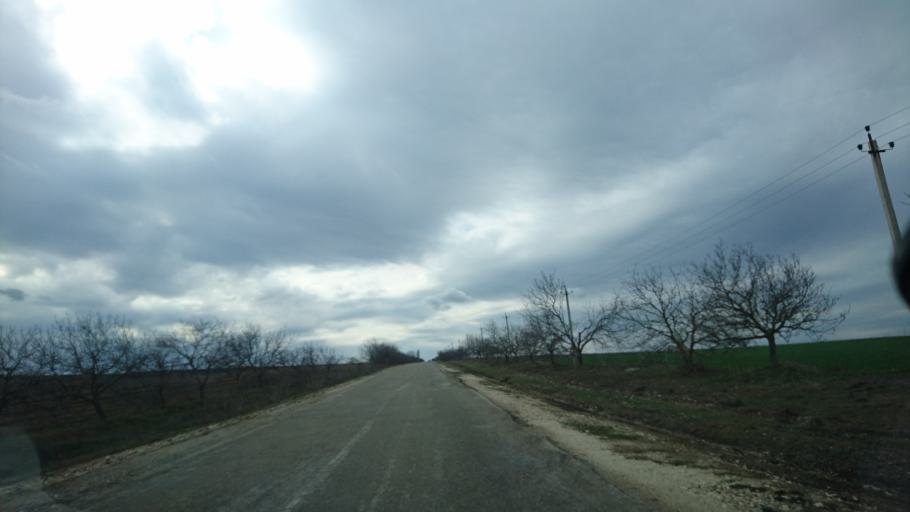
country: MD
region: Cantemir
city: Visniovca
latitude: 46.3236
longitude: 28.4949
